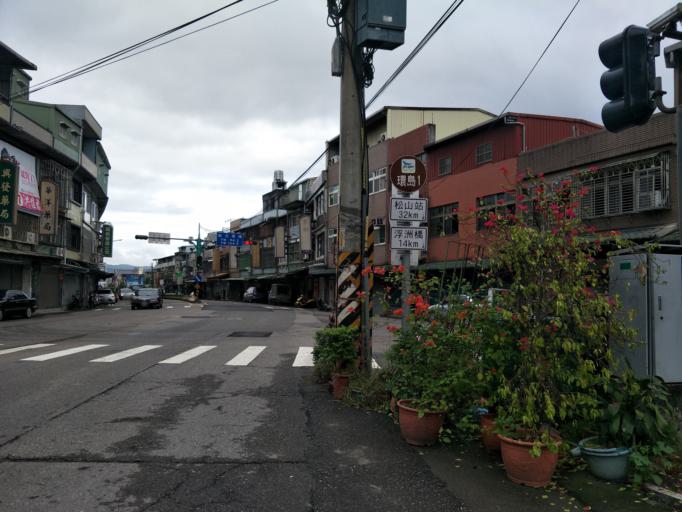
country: TW
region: Taiwan
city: Daxi
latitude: 24.9099
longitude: 121.3659
